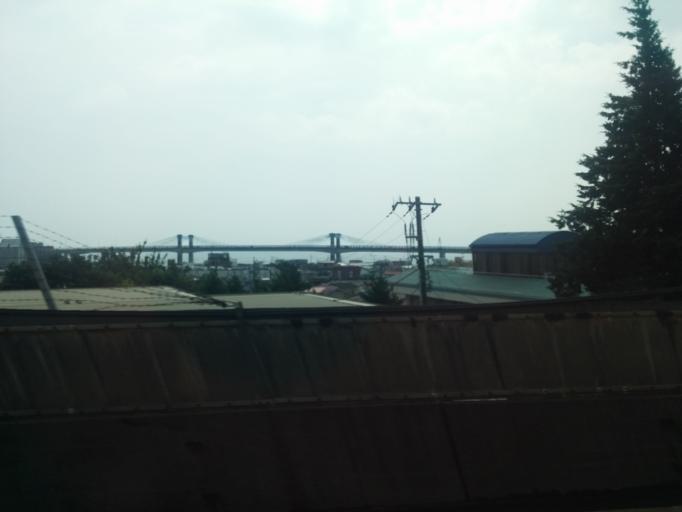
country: JP
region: Kanagawa
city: Odawara
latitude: 35.2396
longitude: 139.1435
